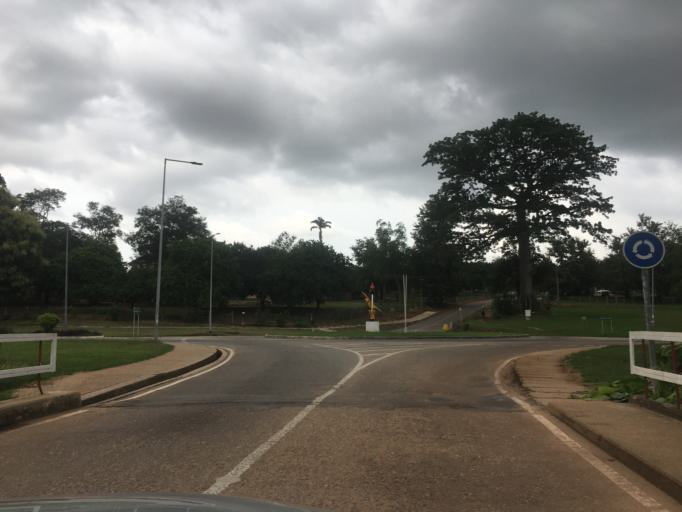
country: GH
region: Ashanti
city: Mamponteng
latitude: 6.6848
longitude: -1.5709
